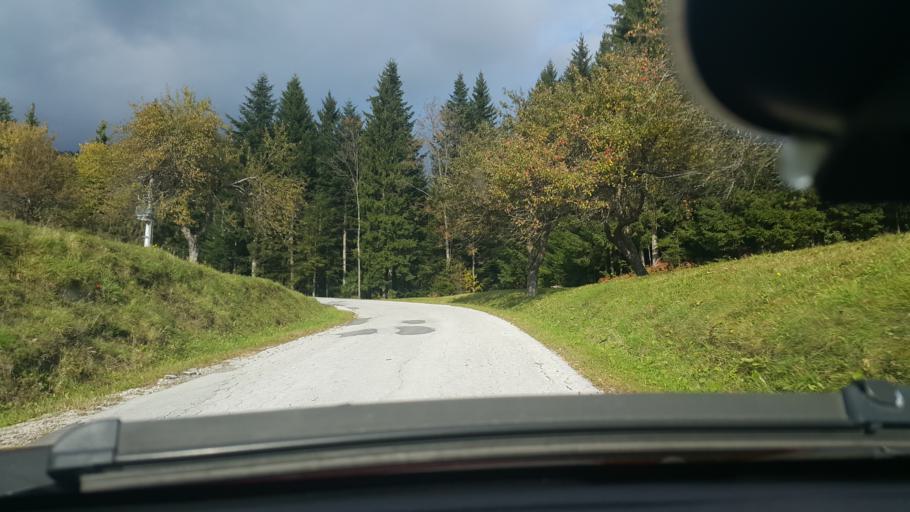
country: SI
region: Vitanje
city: Vitanje
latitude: 46.4163
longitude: 15.2765
